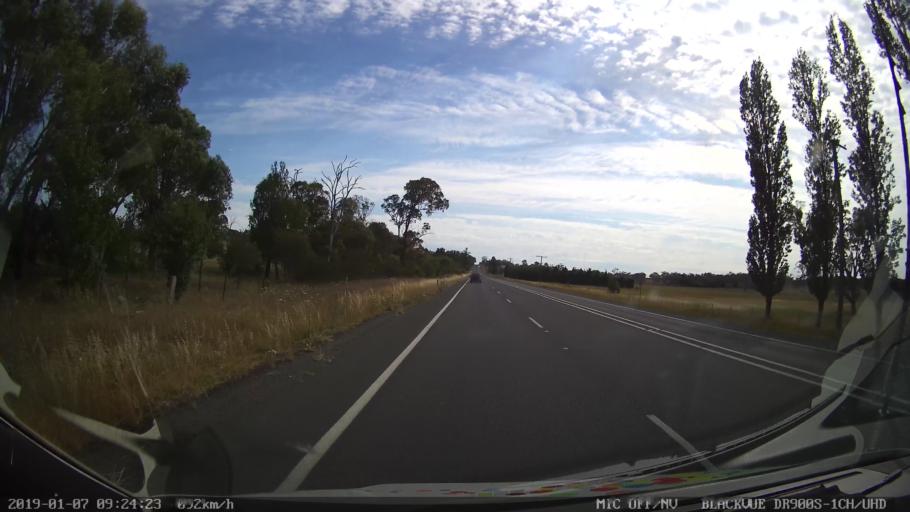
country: AU
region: New South Wales
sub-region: Armidale Dumaresq
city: Armidale
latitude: -30.5478
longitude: 151.5958
